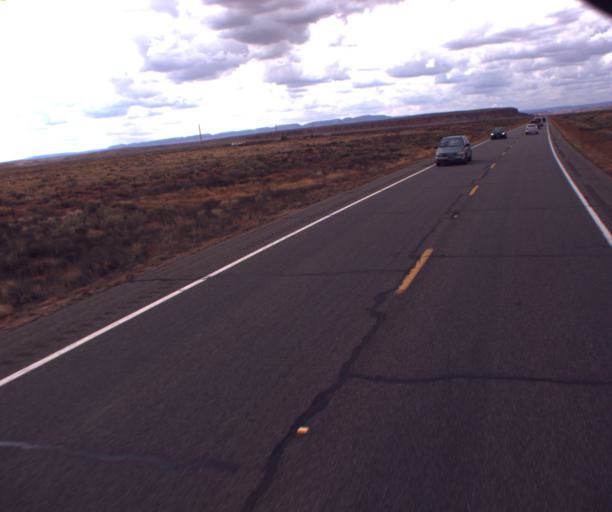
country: US
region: Arizona
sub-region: Navajo County
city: Kayenta
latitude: 36.7867
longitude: -109.9586
